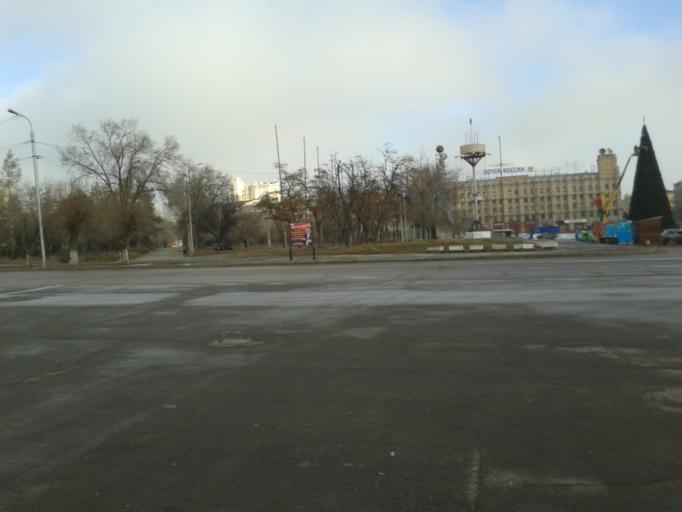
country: RU
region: Volgograd
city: Volgograd
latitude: 48.7082
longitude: 44.5126
